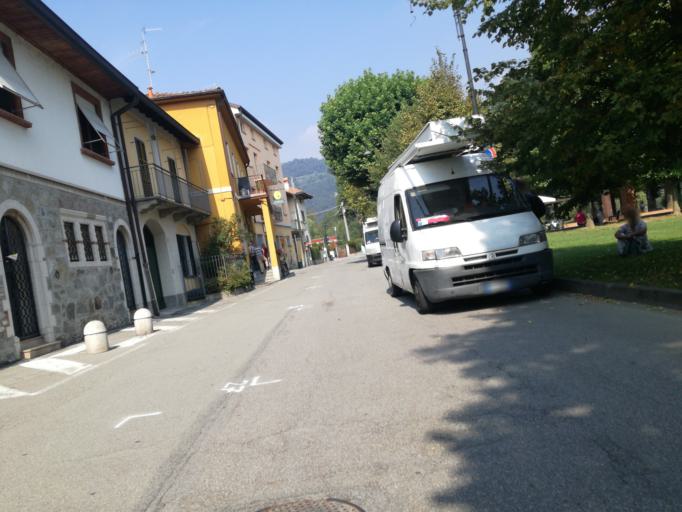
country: IT
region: Lombardy
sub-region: Provincia di Lecco
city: Brivio
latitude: 45.7427
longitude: 9.4499
